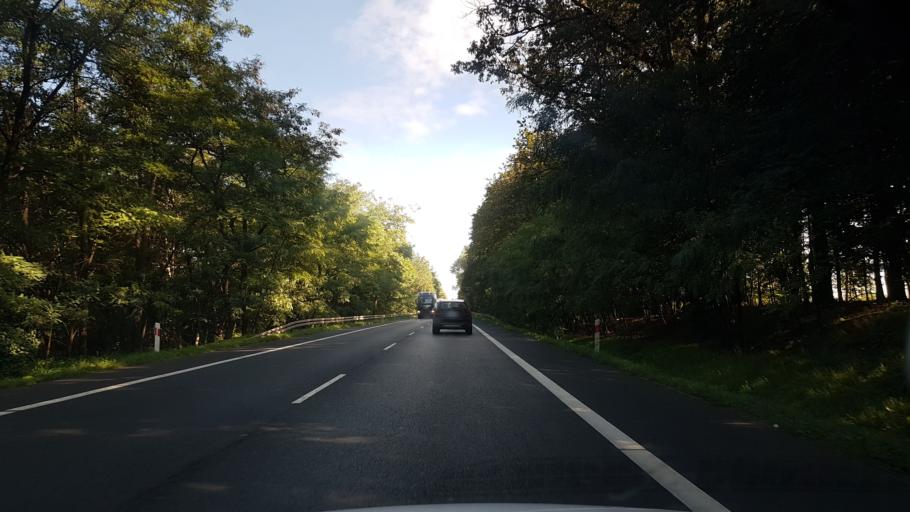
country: PL
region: Greater Poland Voivodeship
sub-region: Powiat koscianski
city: Czempin
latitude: 52.1662
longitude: 16.6978
